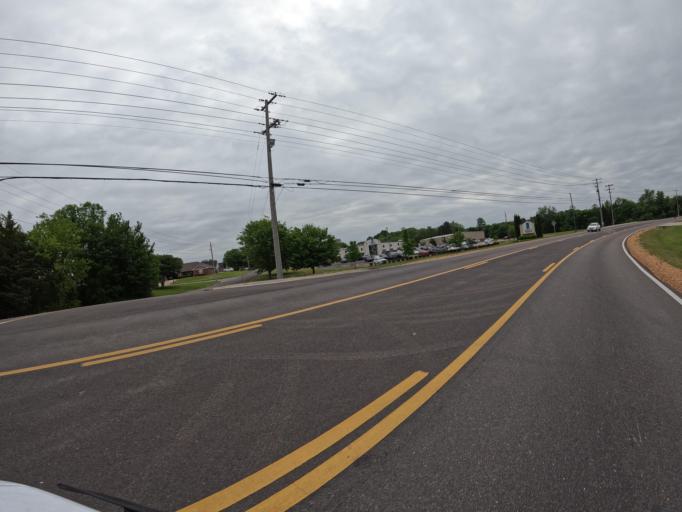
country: US
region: Mississippi
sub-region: Lee County
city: Tupelo
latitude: 34.2810
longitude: -88.7648
